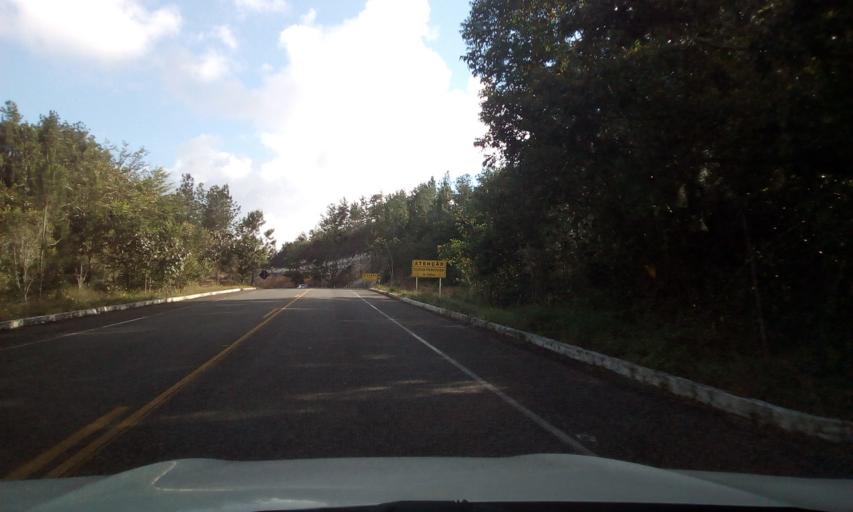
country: BR
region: Bahia
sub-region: Conde
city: Conde
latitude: -12.0970
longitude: -37.7743
